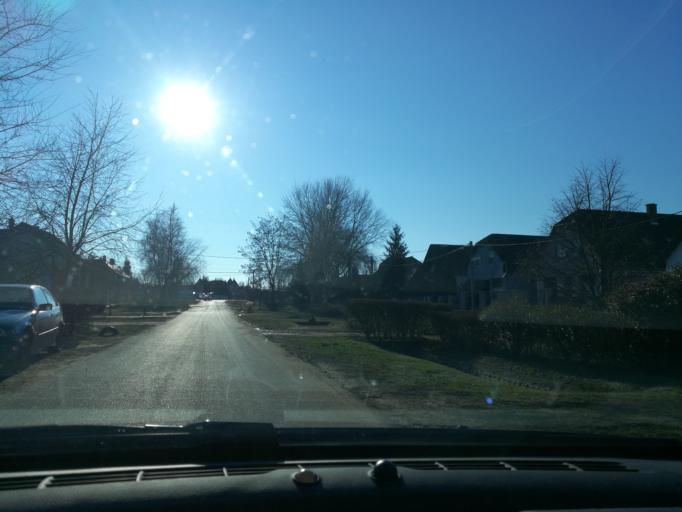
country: HU
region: Szabolcs-Szatmar-Bereg
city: Nyiregyhaza
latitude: 47.9390
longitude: 21.7502
